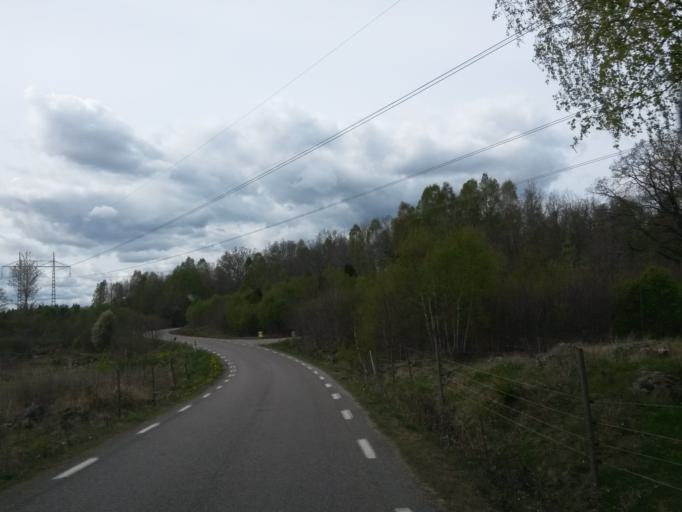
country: SE
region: Vaestra Goetaland
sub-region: Herrljunga Kommun
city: Herrljunga
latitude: 58.1422
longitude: 13.0480
